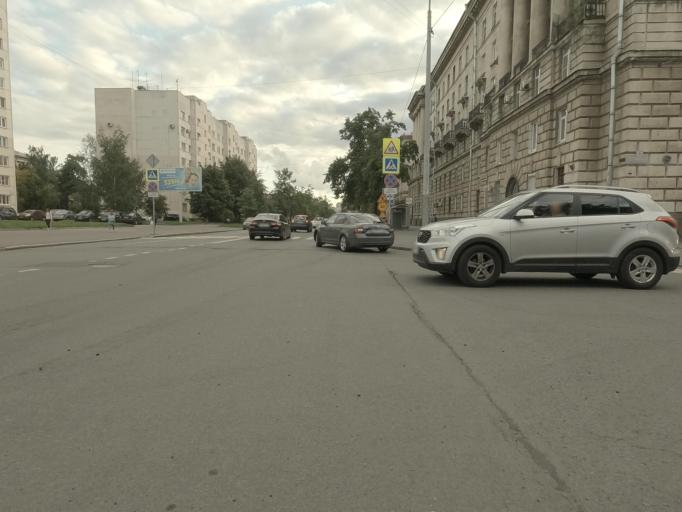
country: RU
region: St.-Petersburg
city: Avtovo
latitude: 59.8679
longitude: 30.2679
